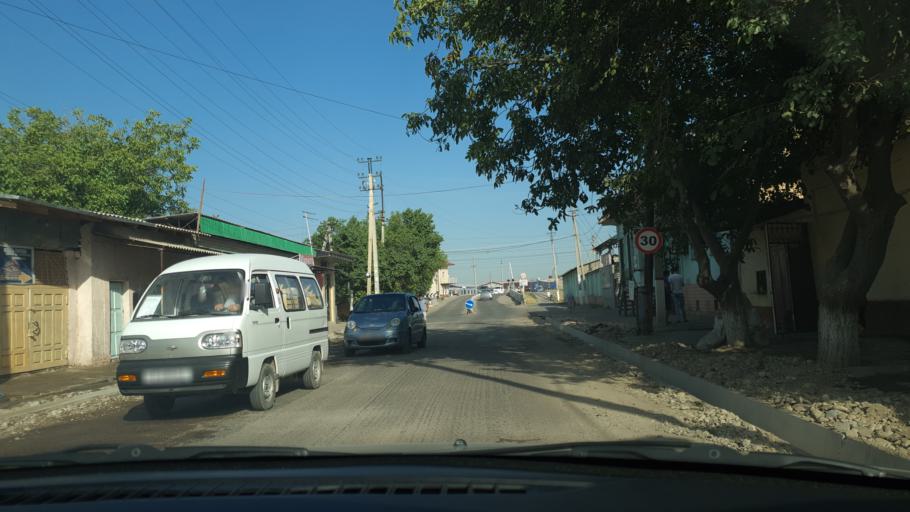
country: UZ
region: Toshkent
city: Urtaowul
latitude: 41.2007
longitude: 69.1570
